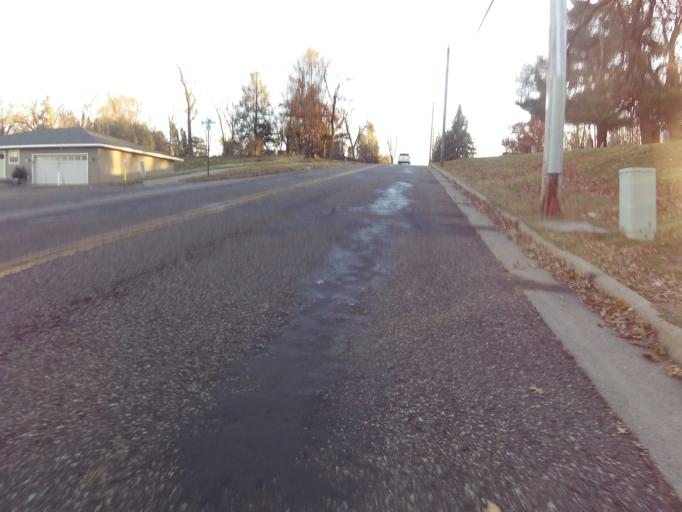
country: US
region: Wisconsin
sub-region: Saint Croix County
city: Hudson
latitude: 44.9756
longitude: -92.7465
